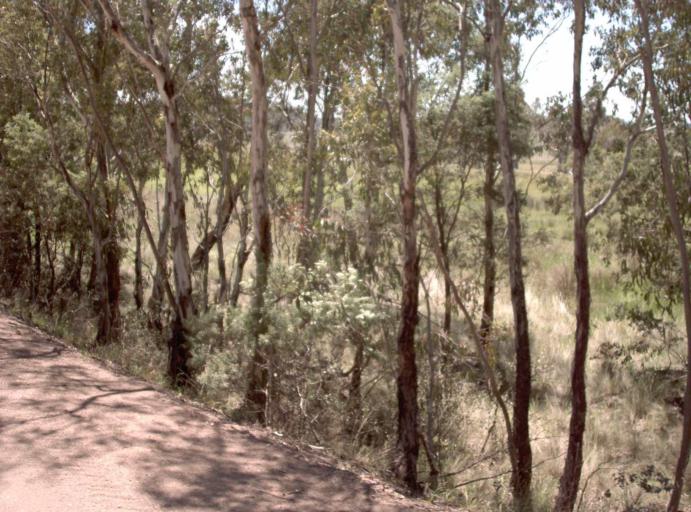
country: AU
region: New South Wales
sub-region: Snowy River
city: Jindabyne
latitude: -37.0247
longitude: 148.2736
